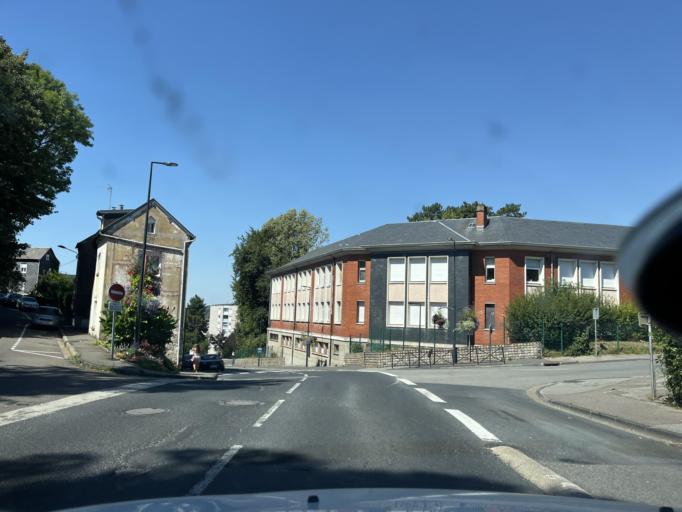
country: FR
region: Haute-Normandie
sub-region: Departement de la Seine-Maritime
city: Lillebonne
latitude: 49.5190
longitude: 0.5399
